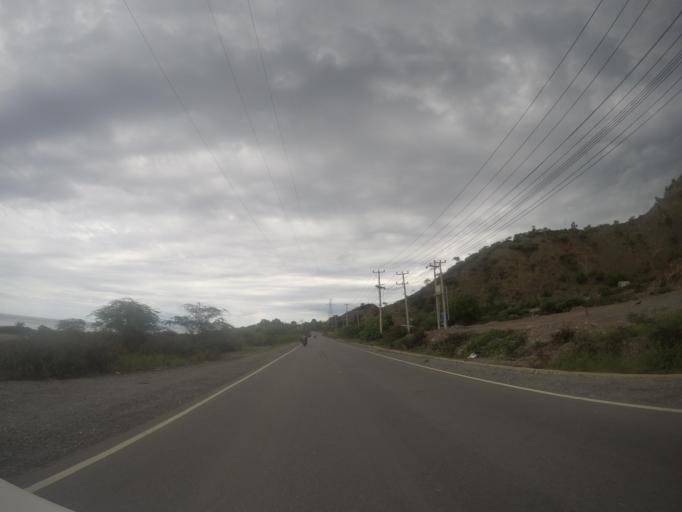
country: TL
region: Liquica
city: Liquica
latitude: -8.5741
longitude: 125.3758
